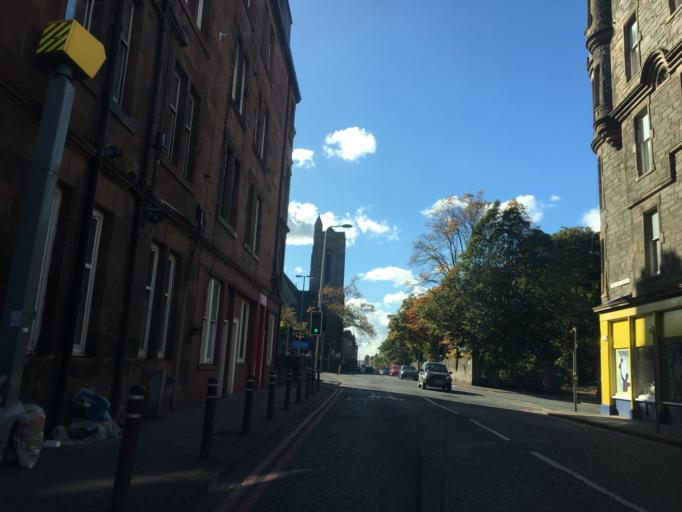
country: GB
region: Scotland
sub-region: Edinburgh
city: Edinburgh
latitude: 55.9375
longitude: -3.2258
